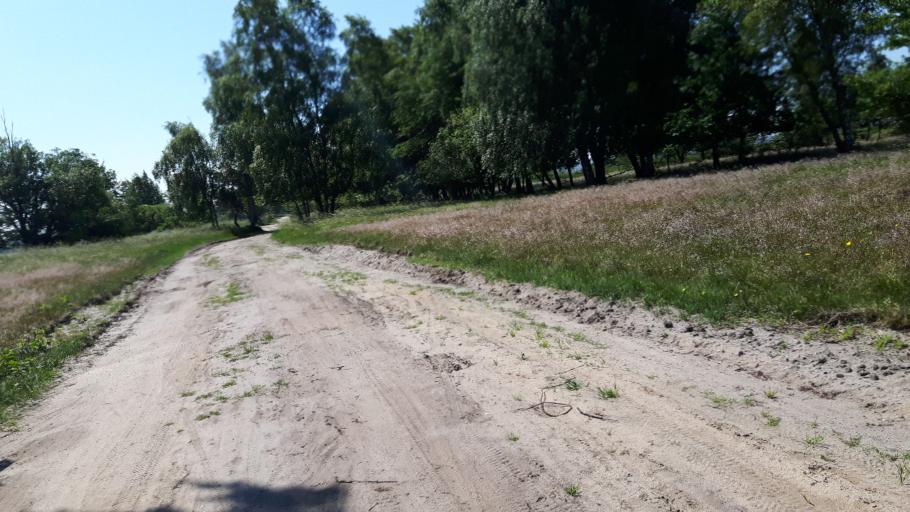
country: PL
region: Pomeranian Voivodeship
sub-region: Powiat slupski
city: Smoldzino
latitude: 54.6706
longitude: 17.1596
